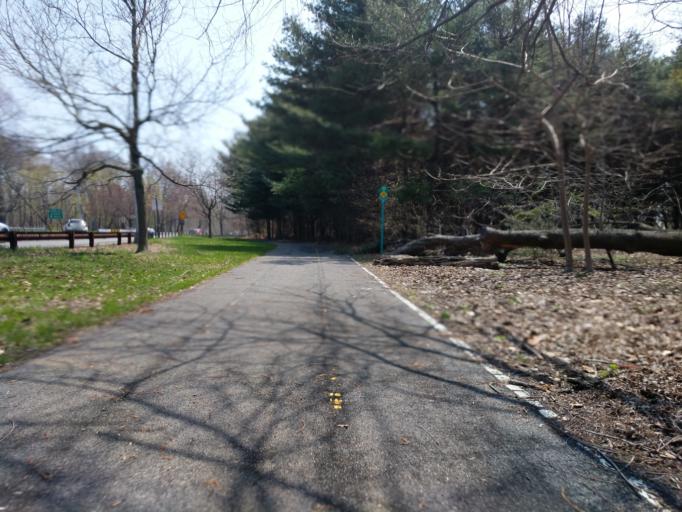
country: US
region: New York
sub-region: Westchester County
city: Pelham Manor
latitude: 40.8605
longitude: -73.8033
